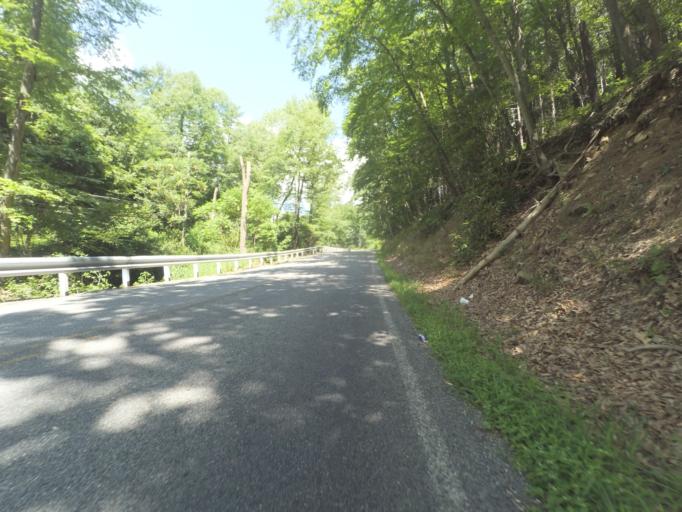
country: US
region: Pennsylvania
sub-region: Centre County
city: Stormstown
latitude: 40.7830
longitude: -78.0480
